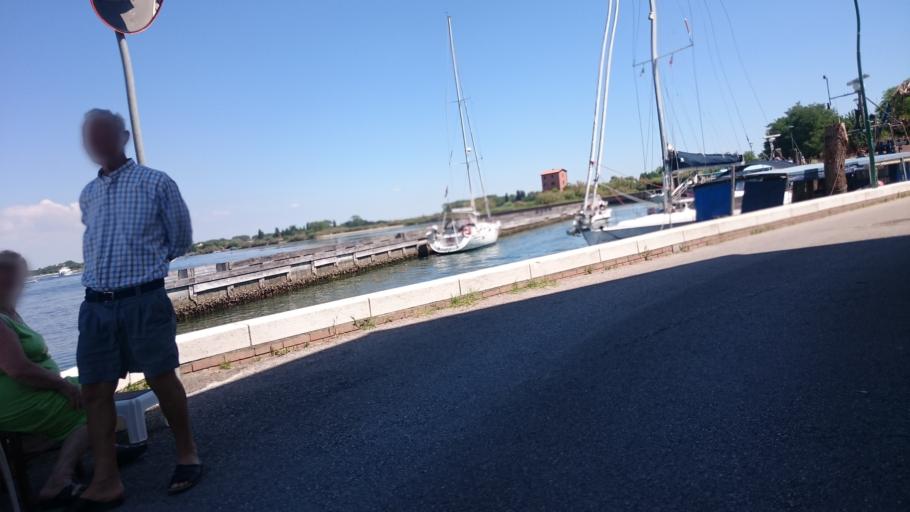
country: IT
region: Veneto
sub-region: Provincia di Venezia
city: San Pietro in Volta
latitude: 45.3238
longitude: 12.3177
